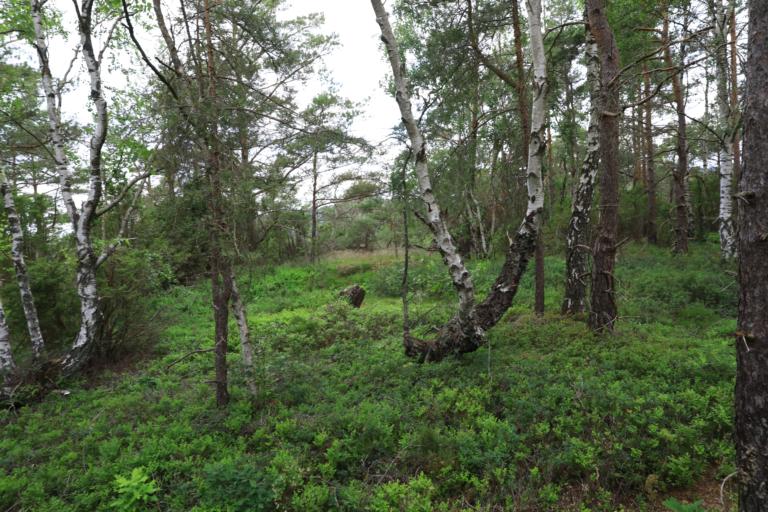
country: SE
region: Halland
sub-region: Varbergs Kommun
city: Varberg
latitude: 57.1726
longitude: 12.2566
